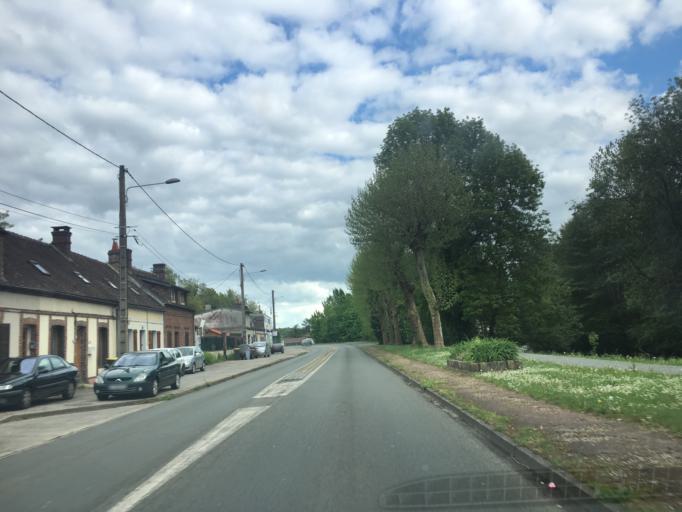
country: FR
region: Centre
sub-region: Departement d'Eure-et-Loir
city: Saint-Lubin-des-Joncherets
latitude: 48.7661
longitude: 1.2092
